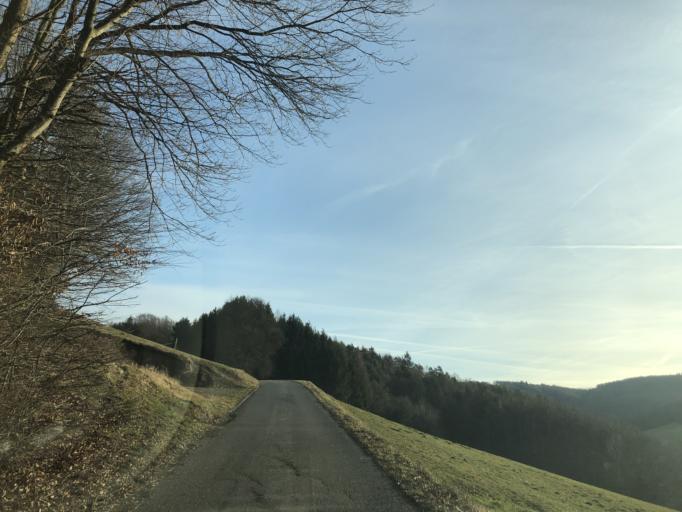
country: AT
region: Lower Austria
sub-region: Politischer Bezirk Sankt Polten
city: Kasten bei Boheimkirchen
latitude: 48.1122
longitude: 15.7620
